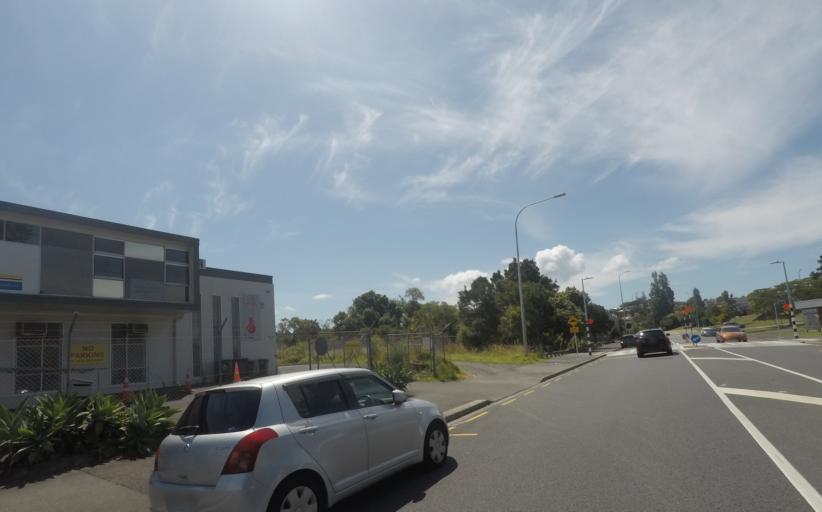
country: NZ
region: Auckland
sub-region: Auckland
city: Tamaki
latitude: -36.8734
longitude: 174.8533
